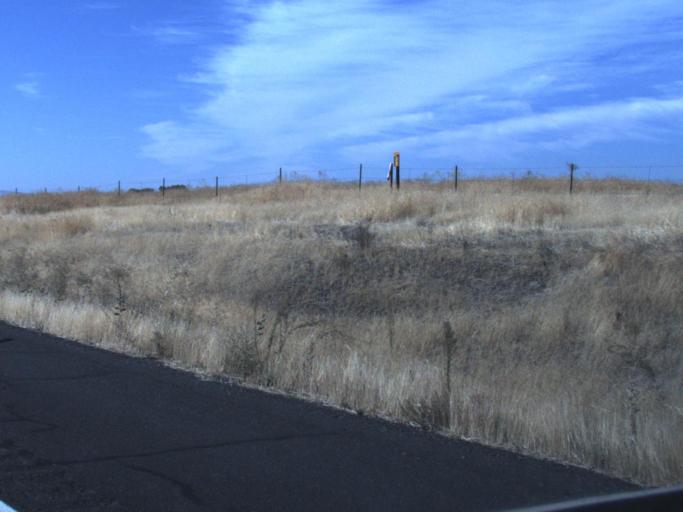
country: US
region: Washington
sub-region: Franklin County
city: Pasco
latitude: 46.4126
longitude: -119.0478
